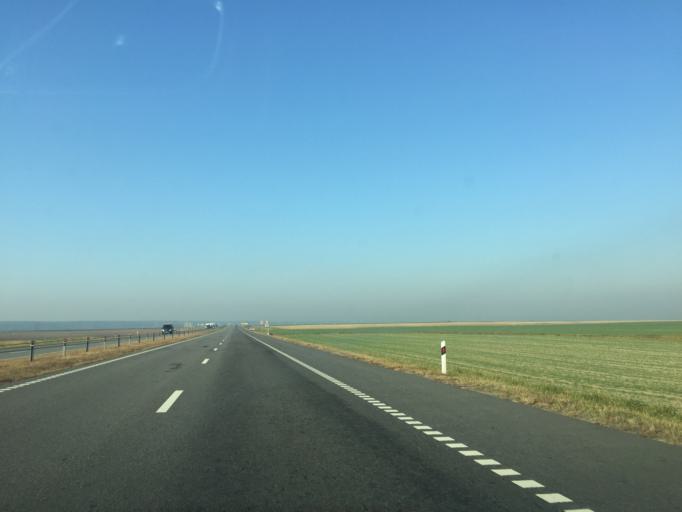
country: BY
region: Gomel
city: Kastsyukowka
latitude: 52.4873
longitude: 30.7914
